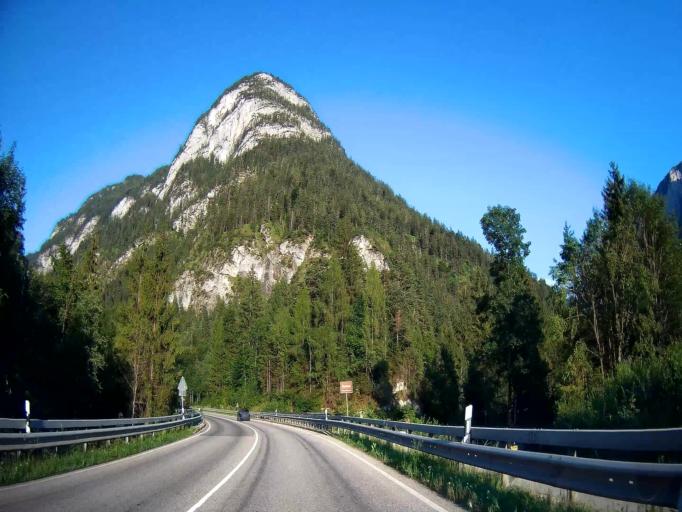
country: DE
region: Bavaria
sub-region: Upper Bavaria
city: Schneizlreuth
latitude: 47.6793
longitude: 12.8276
